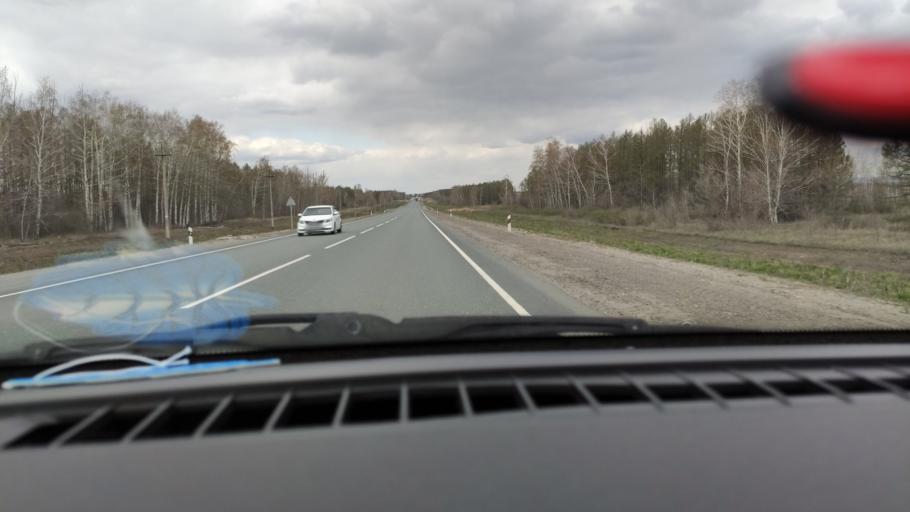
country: RU
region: Saratov
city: Shikhany
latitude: 52.1540
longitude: 47.1815
